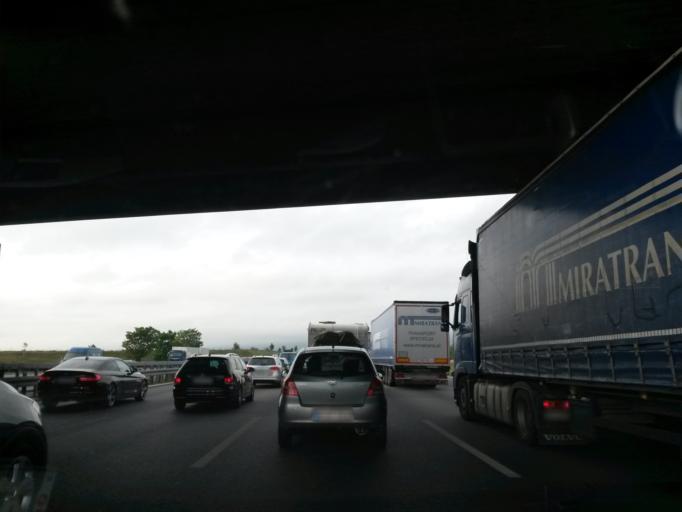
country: DE
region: Bavaria
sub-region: Upper Bavaria
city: Garching bei Munchen
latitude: 48.2642
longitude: 11.6463
